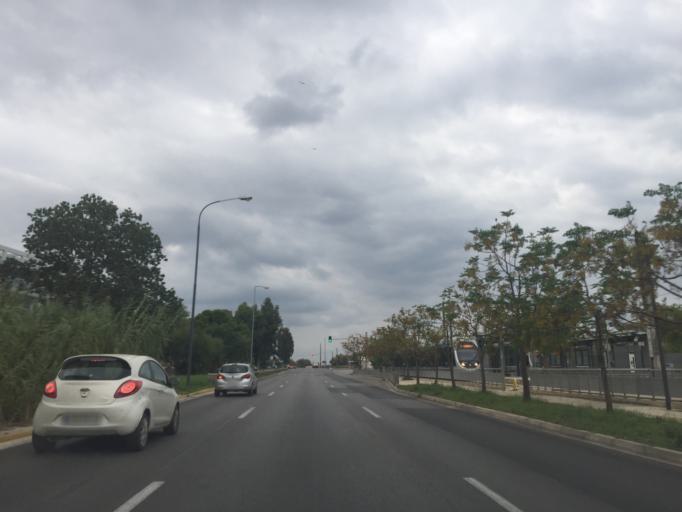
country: GR
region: Attica
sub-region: Nomarchia Athinas
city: Glyfada
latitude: 37.8503
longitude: 23.7526
